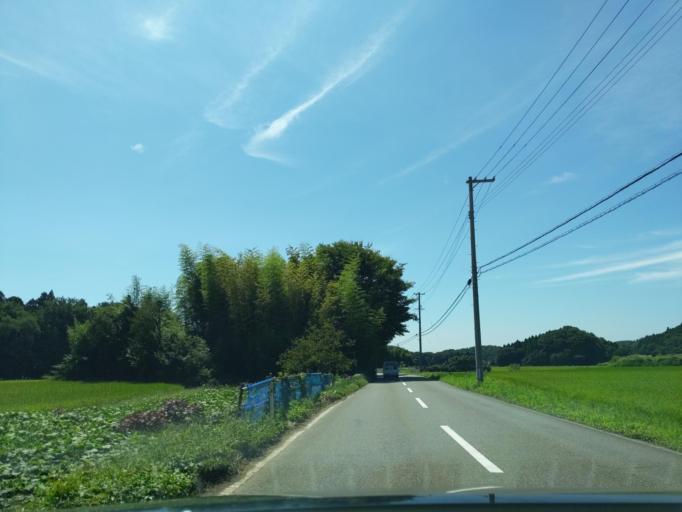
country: JP
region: Fukushima
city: Koriyama
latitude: 37.3836
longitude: 140.2611
